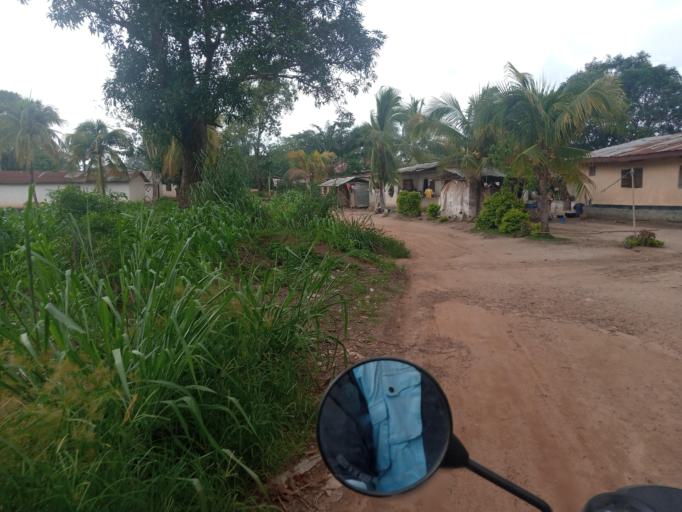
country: SL
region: Southern Province
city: Bo
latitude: 7.9885
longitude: -11.7429
